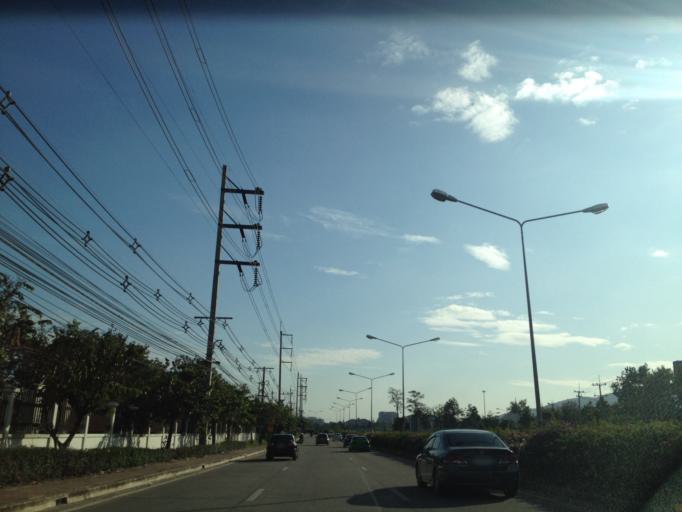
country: TH
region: Chiang Mai
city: Chiang Mai
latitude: 18.8345
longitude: 98.9638
